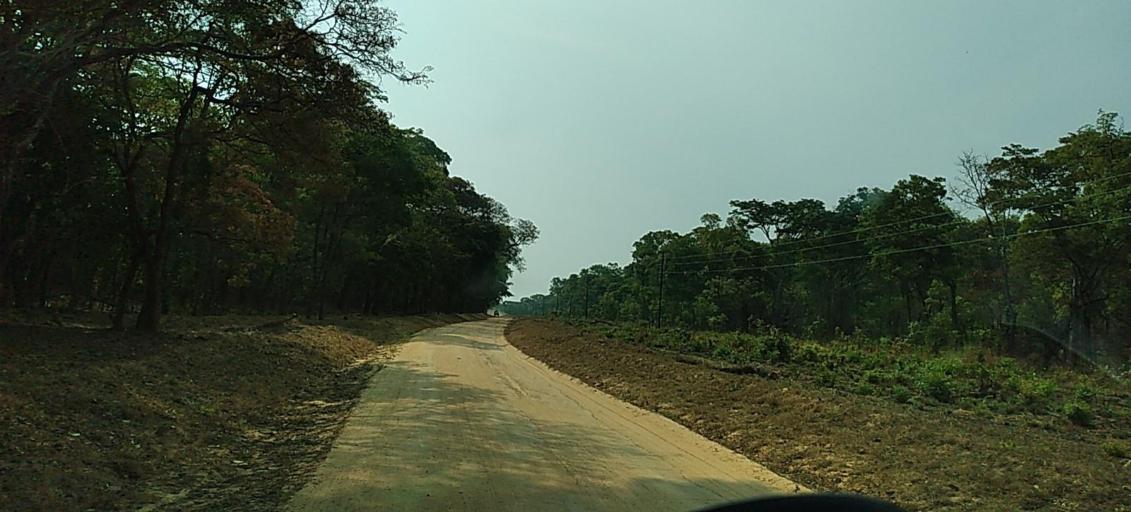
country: ZM
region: North-Western
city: Solwezi
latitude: -12.6906
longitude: 26.4001
